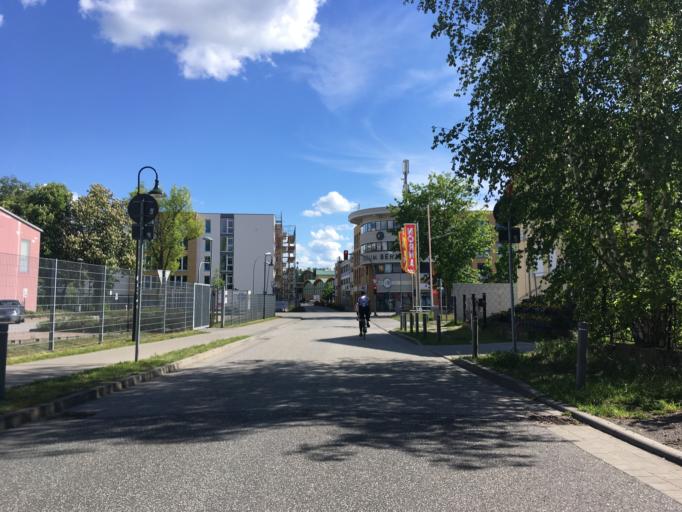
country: DE
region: Brandenburg
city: Bernau bei Berlin
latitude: 52.6756
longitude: 13.5737
